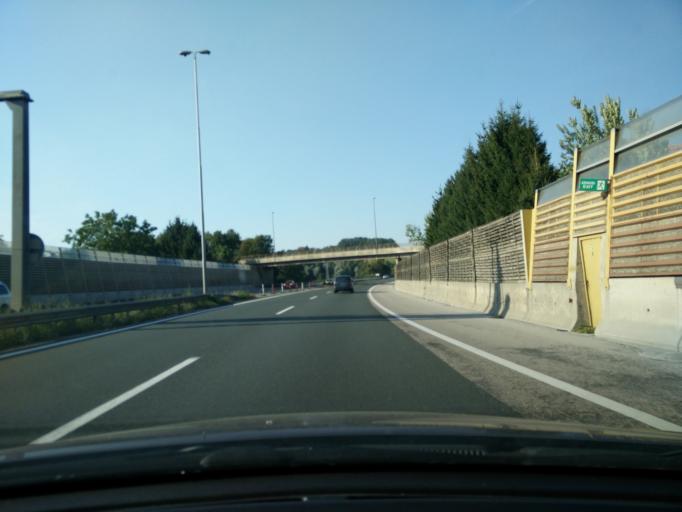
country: SI
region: Brezovica
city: Vnanje Gorice
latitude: 46.0429
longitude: 14.4471
